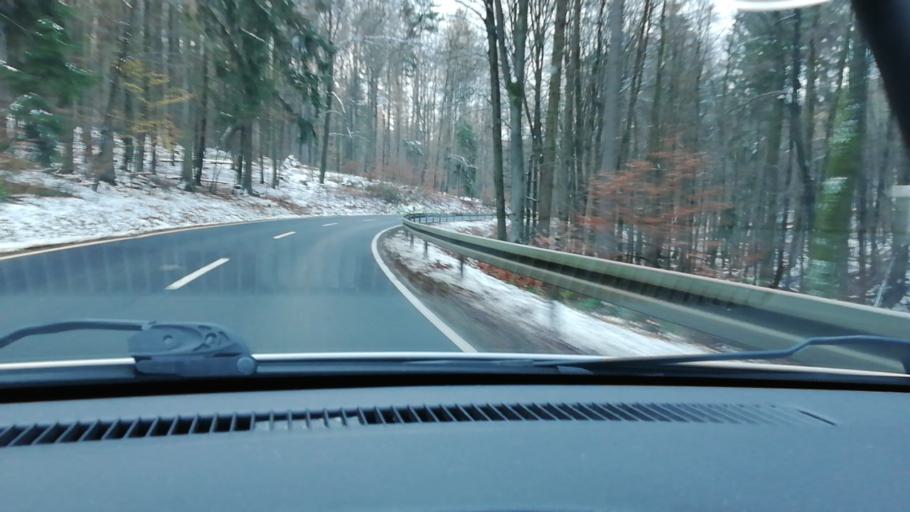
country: DE
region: Bavaria
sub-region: Regierungsbezirk Unterfranken
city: Geiselbach
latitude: 50.1329
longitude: 9.1851
